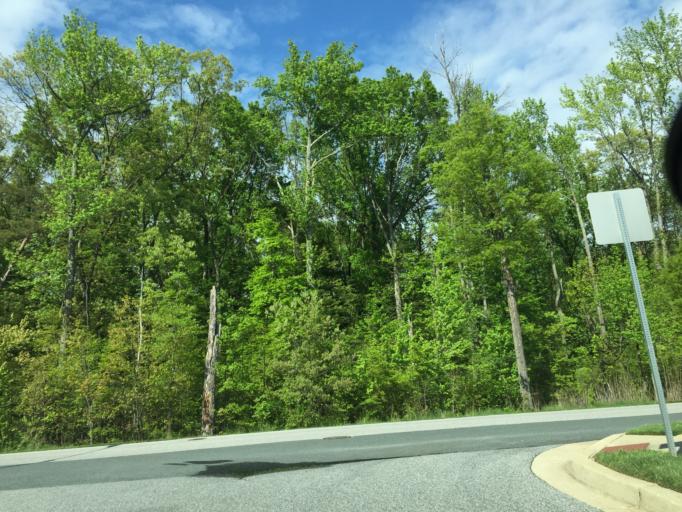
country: US
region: Maryland
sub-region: Baltimore County
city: Middle River
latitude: 39.3161
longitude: -76.4396
